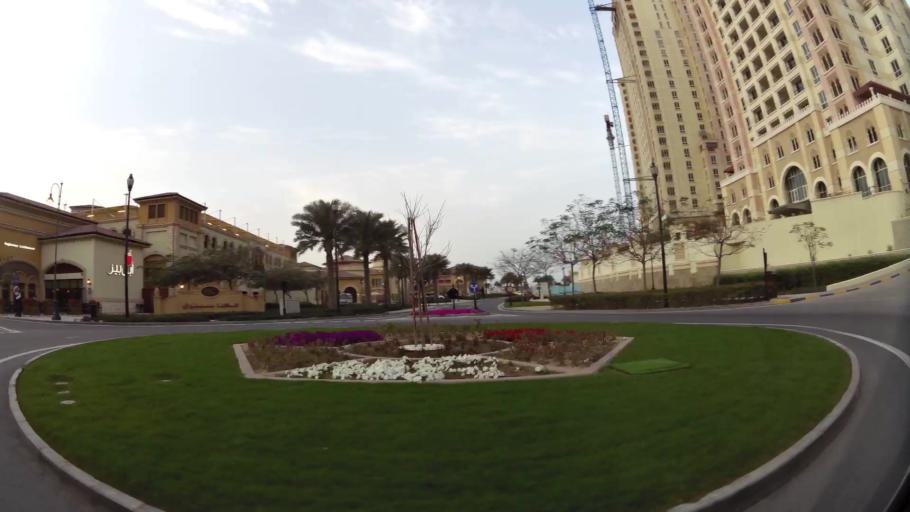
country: QA
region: Baladiyat ad Dawhah
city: Doha
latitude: 25.3679
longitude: 51.5527
